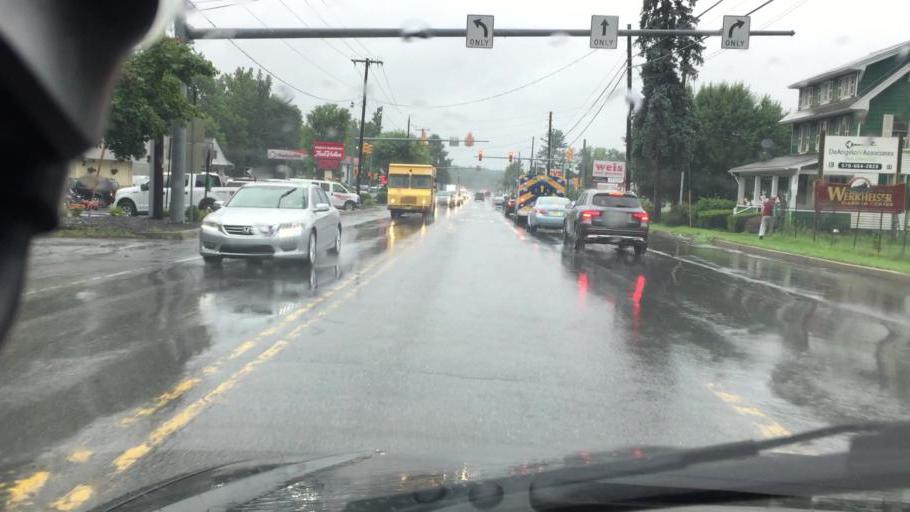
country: US
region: Pennsylvania
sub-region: Monroe County
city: Tannersville
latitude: 41.0417
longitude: -75.3070
